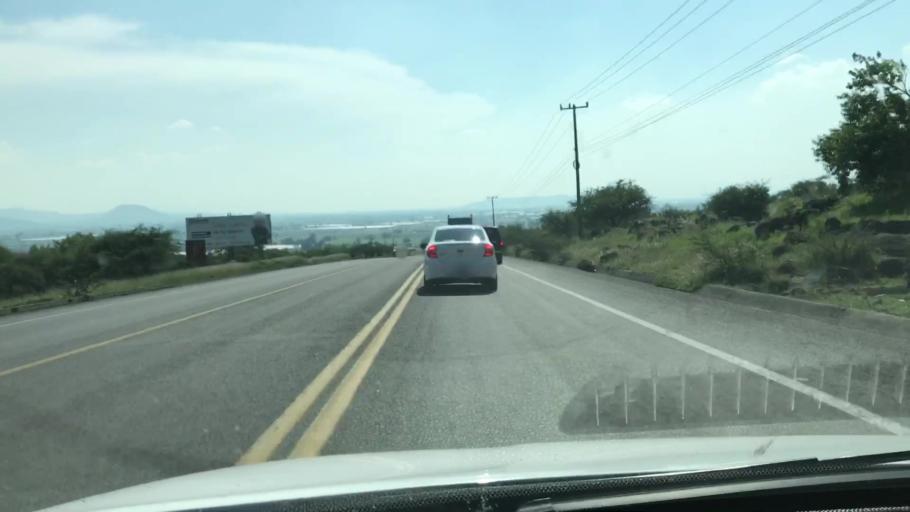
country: MX
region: Michoacan
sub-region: Yurecuaro
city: Yurecuaro
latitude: 20.3311
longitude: -102.2415
